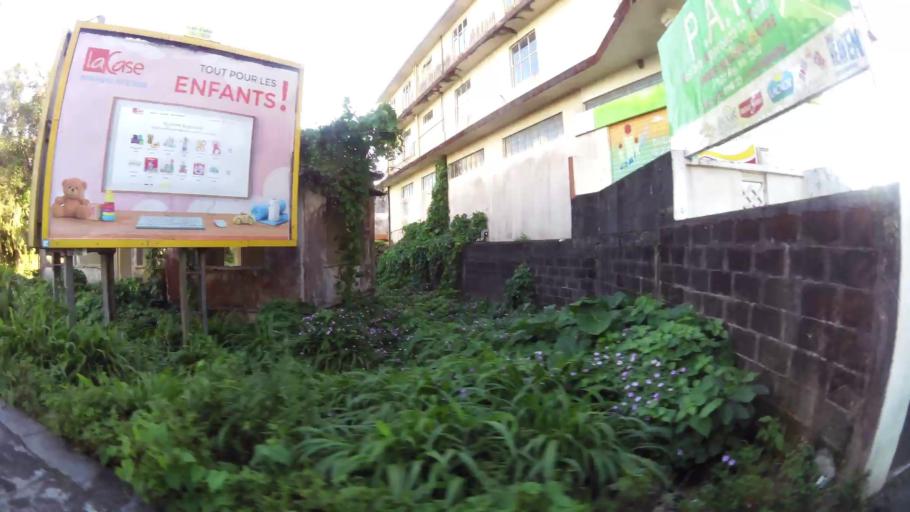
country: MU
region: Plaines Wilhems
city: Curepipe
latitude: -20.3100
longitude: 57.5245
